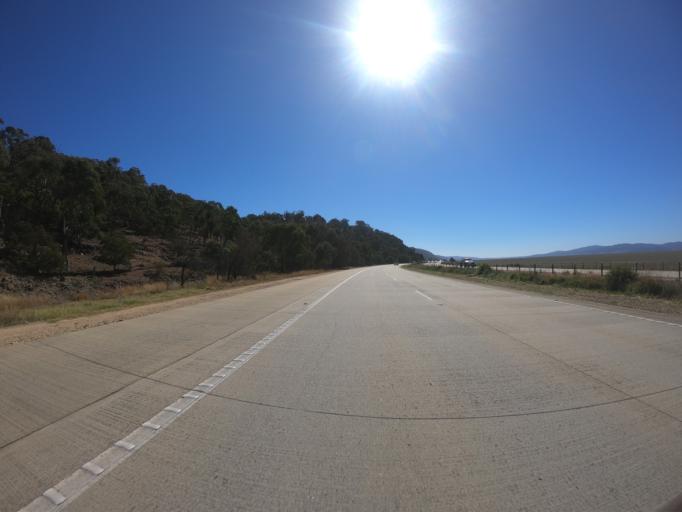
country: AU
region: New South Wales
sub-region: Yass Valley
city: Gundaroo
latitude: -35.0893
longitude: 149.3746
